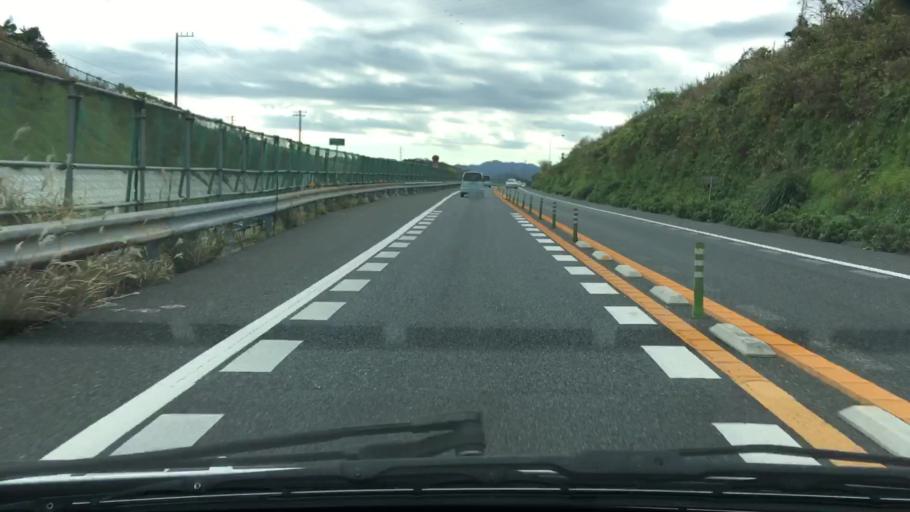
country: JP
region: Chiba
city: Kimitsu
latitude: 35.2401
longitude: 139.8884
